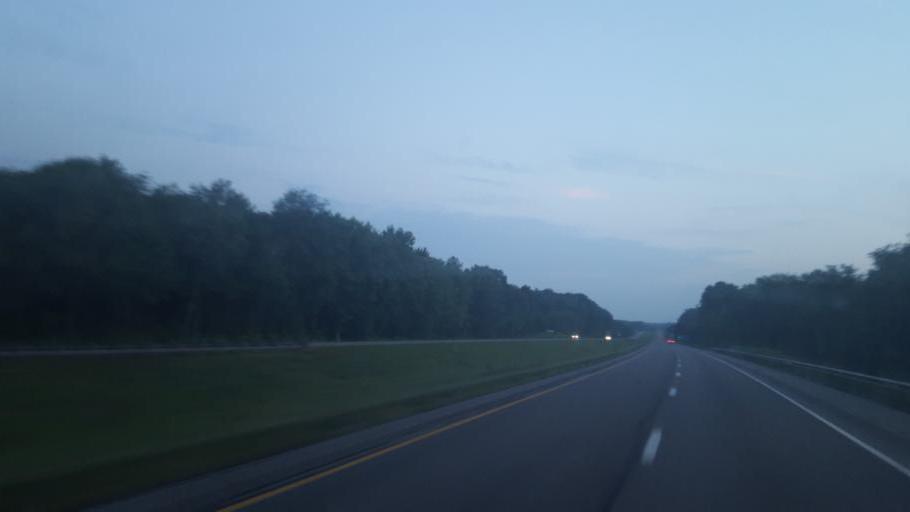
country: US
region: Pennsylvania
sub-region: Mercer County
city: Mercer
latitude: 41.2422
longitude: -80.1604
